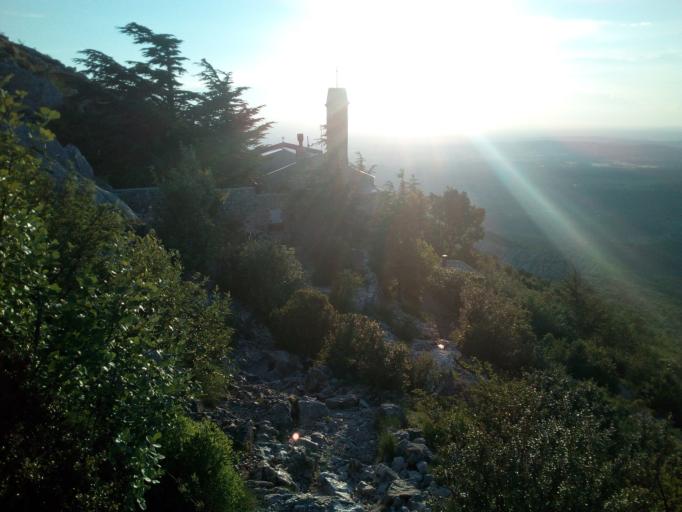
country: FR
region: Provence-Alpes-Cote d'Azur
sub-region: Departement des Bouches-du-Rhone
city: Chateauneuf-le-Rouge
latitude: 43.5317
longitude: 5.5788
